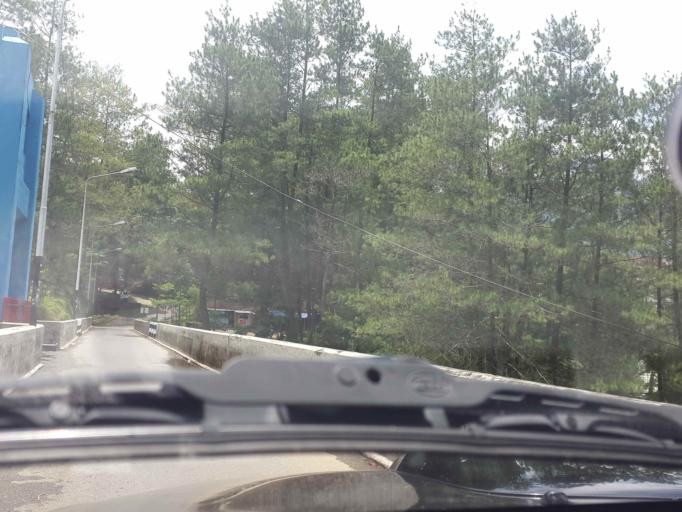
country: ID
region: Central Java
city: Wonosobo
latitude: -7.2735
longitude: 109.9266
